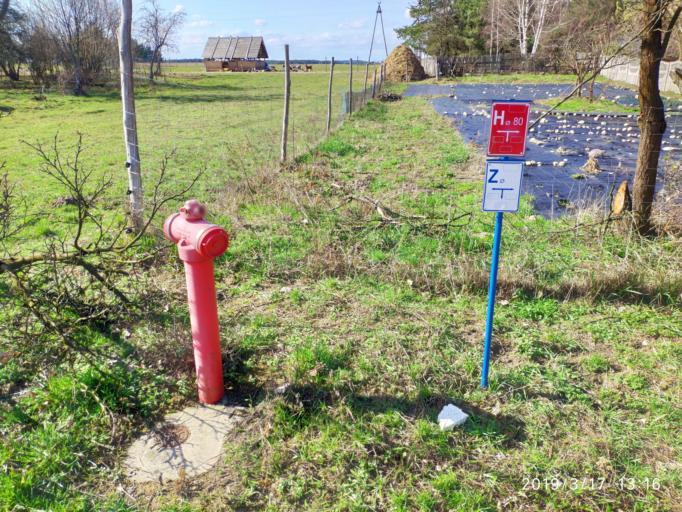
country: PL
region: Lubusz
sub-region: Powiat zielonogorski
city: Bojadla
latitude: 51.9441
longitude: 15.7683
